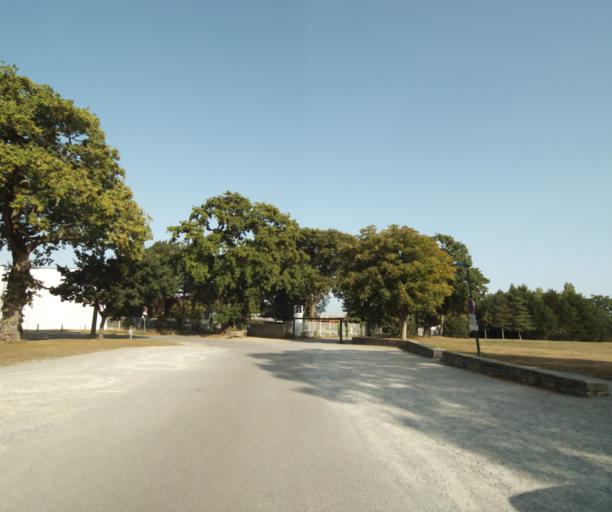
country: FR
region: Brittany
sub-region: Departement du Morbihan
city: Riantec
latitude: 47.7152
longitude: -3.3205
